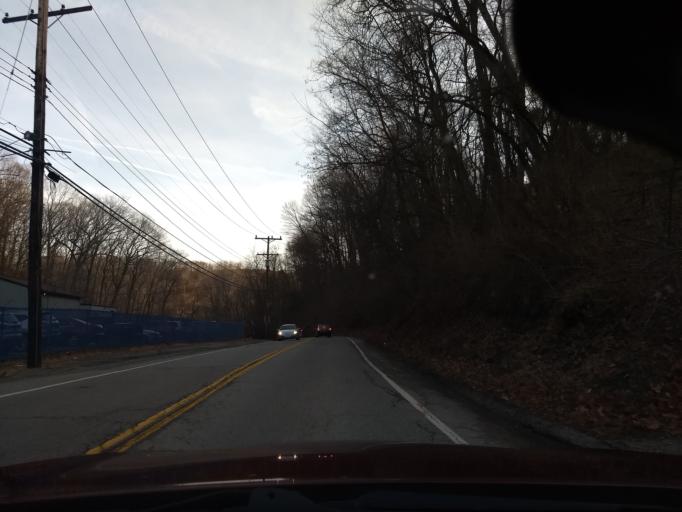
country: US
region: Pennsylvania
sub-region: Allegheny County
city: Brentwood
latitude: 40.3584
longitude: -79.9585
